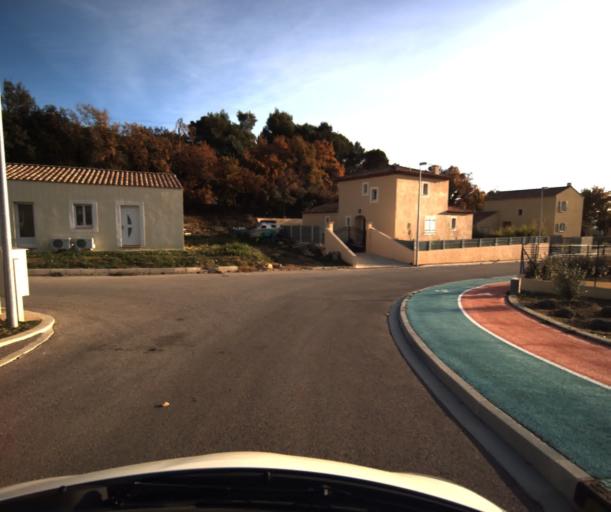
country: FR
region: Provence-Alpes-Cote d'Azur
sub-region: Departement du Vaucluse
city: Pertuis
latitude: 43.6944
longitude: 5.5336
